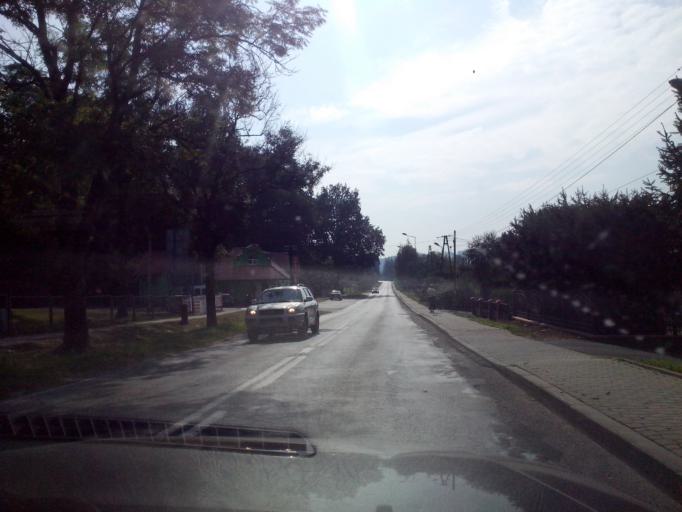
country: PL
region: Subcarpathian Voivodeship
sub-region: Powiat strzyzowski
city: Czudec
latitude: 49.9433
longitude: 21.8450
